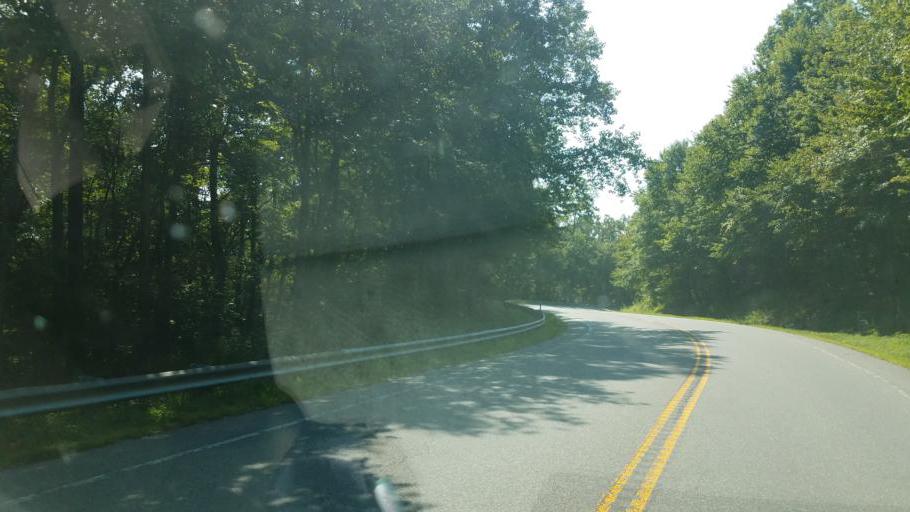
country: US
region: North Carolina
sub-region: Avery County
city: Newland
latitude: 35.9383
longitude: -81.8381
